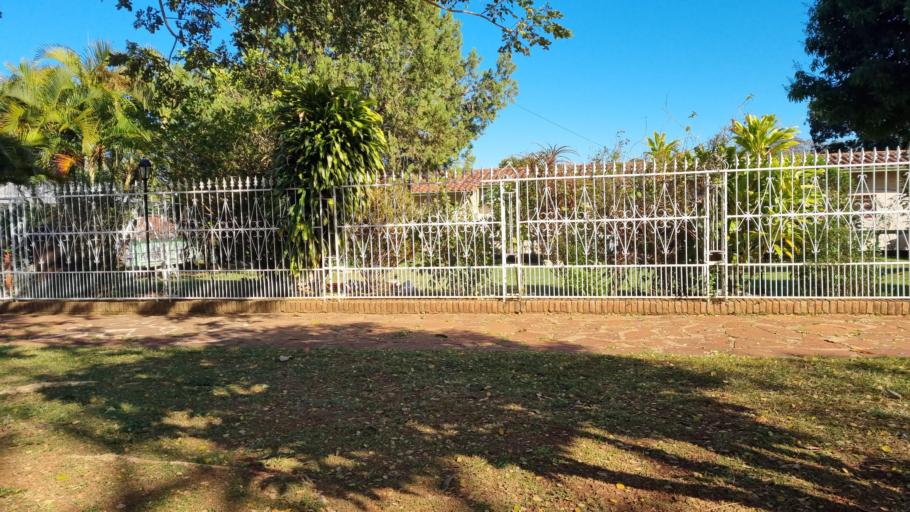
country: PY
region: Misiones
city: San Juan Bautista
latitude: -26.6674
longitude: -57.1369
